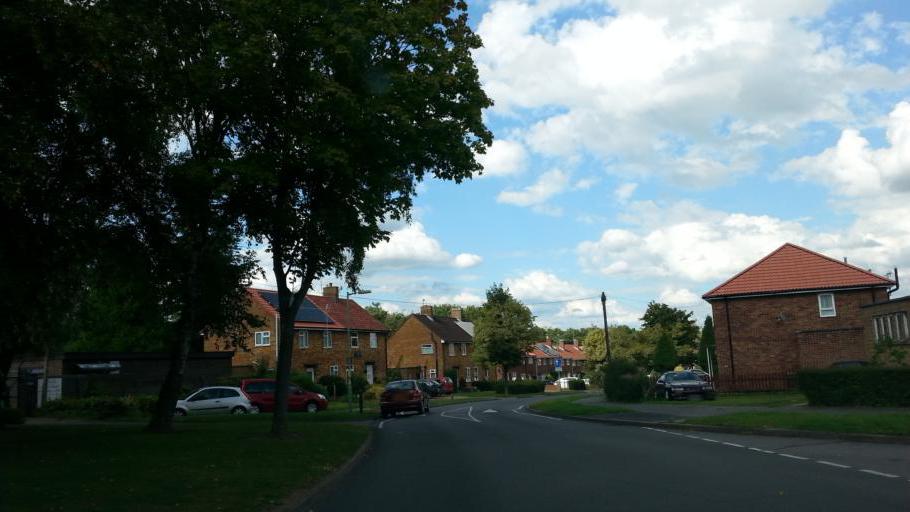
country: GB
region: England
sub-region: Suffolk
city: Bury St Edmunds
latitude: 52.2637
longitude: 0.6984
